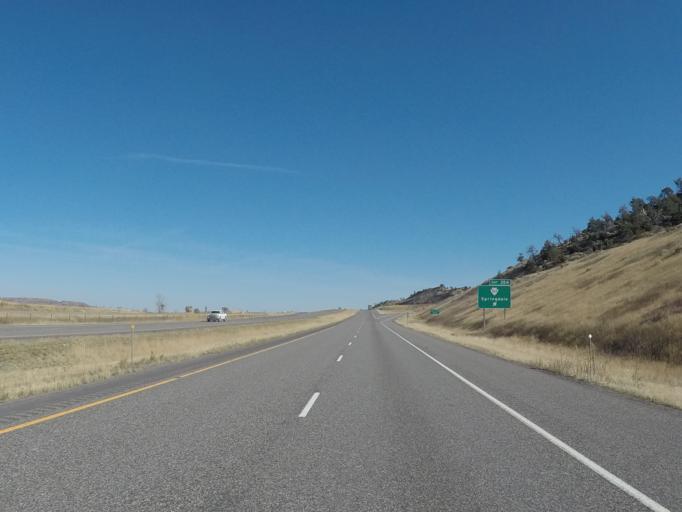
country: US
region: Montana
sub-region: Sweet Grass County
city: Big Timber
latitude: 45.7355
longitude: -110.2224
